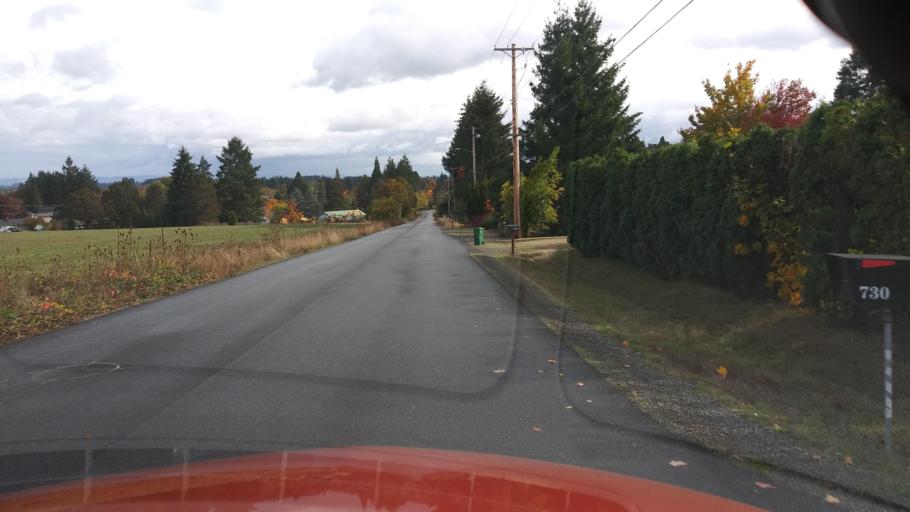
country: US
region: Oregon
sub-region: Washington County
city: Forest Grove
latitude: 45.5329
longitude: -123.1337
